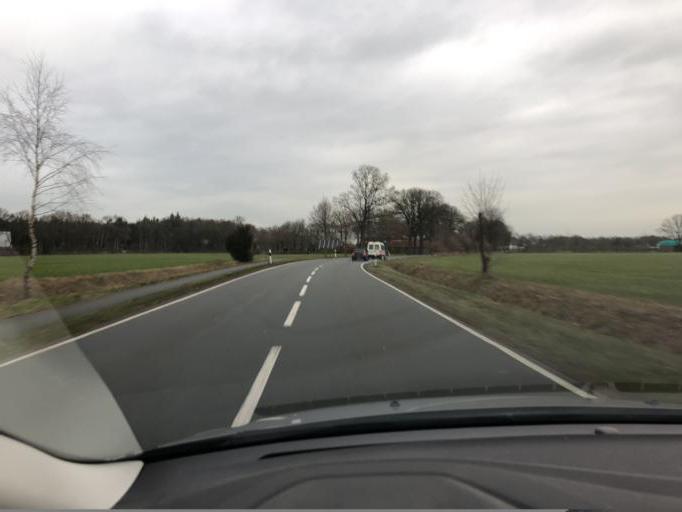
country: DE
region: Lower Saxony
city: Wiefelstede
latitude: 53.1895
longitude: 8.1195
